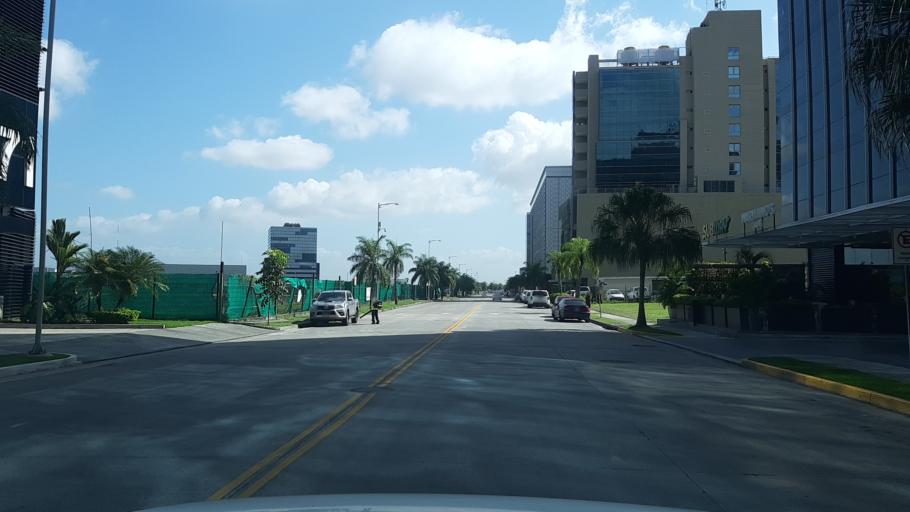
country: PA
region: Panama
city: San Miguelito
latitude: 9.0282
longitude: -79.4622
